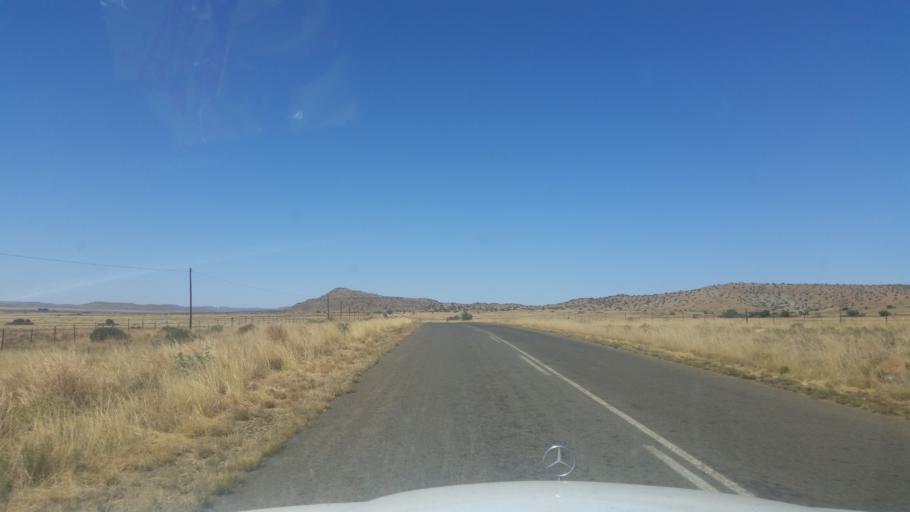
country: ZA
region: Eastern Cape
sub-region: Joe Gqabi District Municipality
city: Burgersdorp
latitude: -30.7190
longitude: 25.7552
